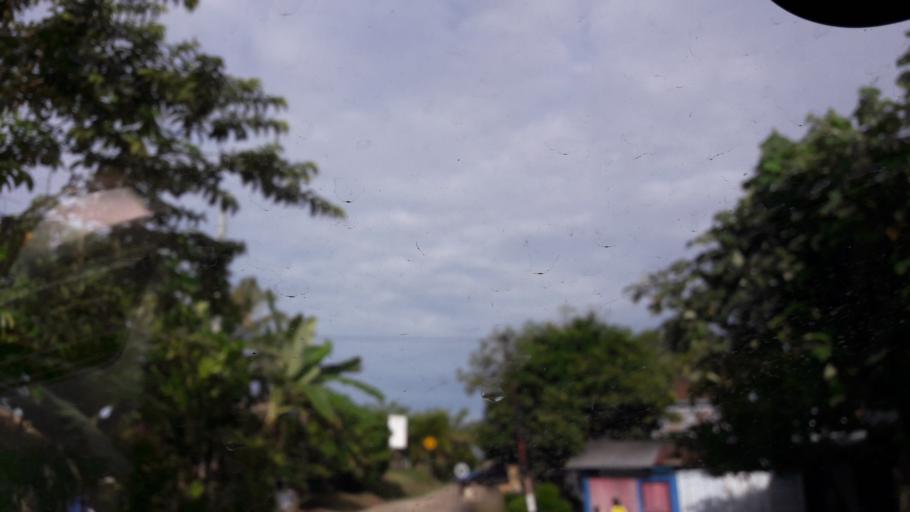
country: ID
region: South Sumatra
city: Gunungmegang Dalam
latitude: -3.2653
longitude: 103.8176
